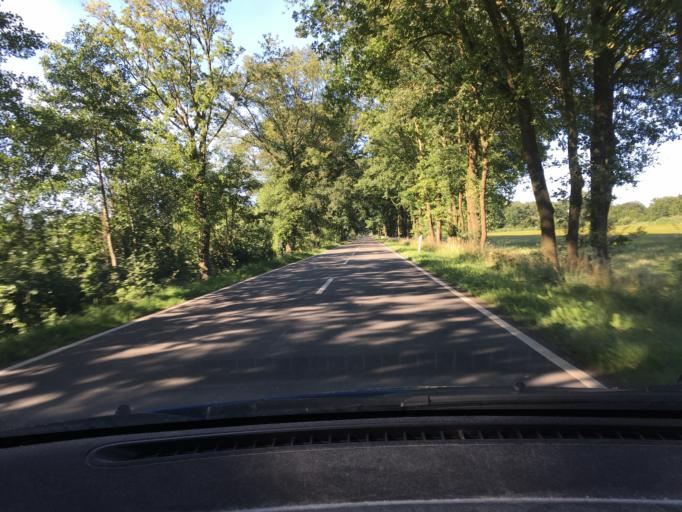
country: DE
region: Mecklenburg-Vorpommern
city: Boizenburg
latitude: 53.3322
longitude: 10.6812
